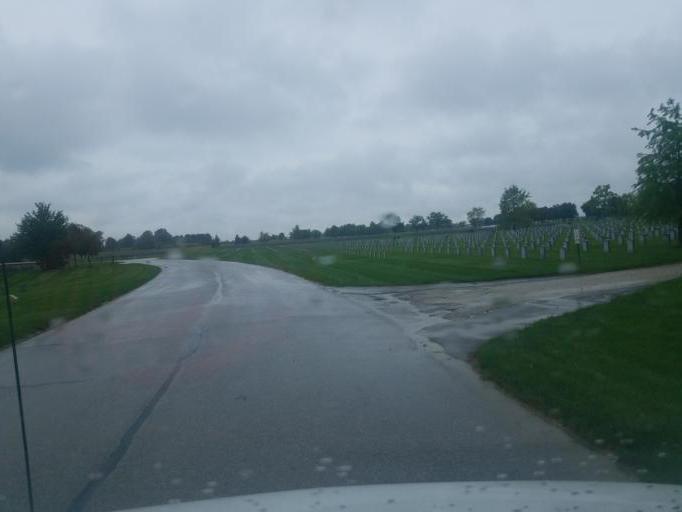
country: US
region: Ohio
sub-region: Wayne County
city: Rittman
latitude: 40.9997
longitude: -81.8098
